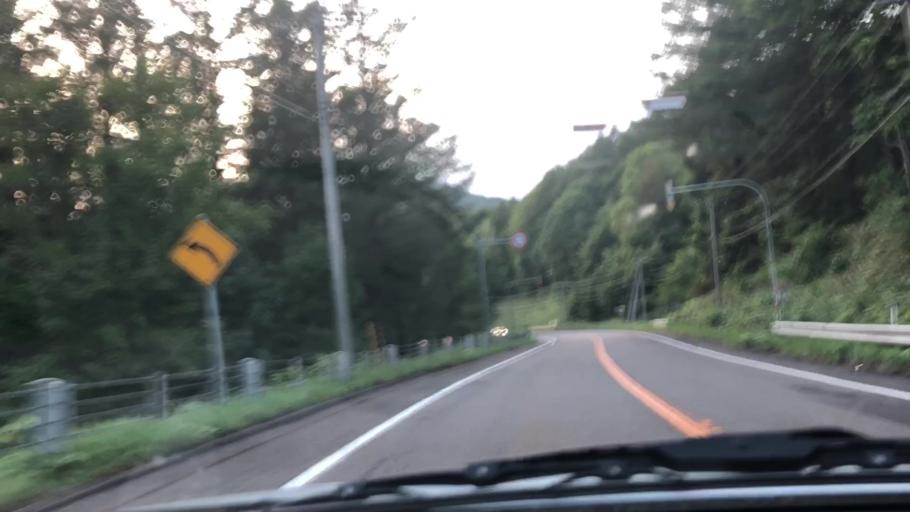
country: JP
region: Hokkaido
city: Shimo-furano
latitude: 42.8913
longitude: 142.1928
